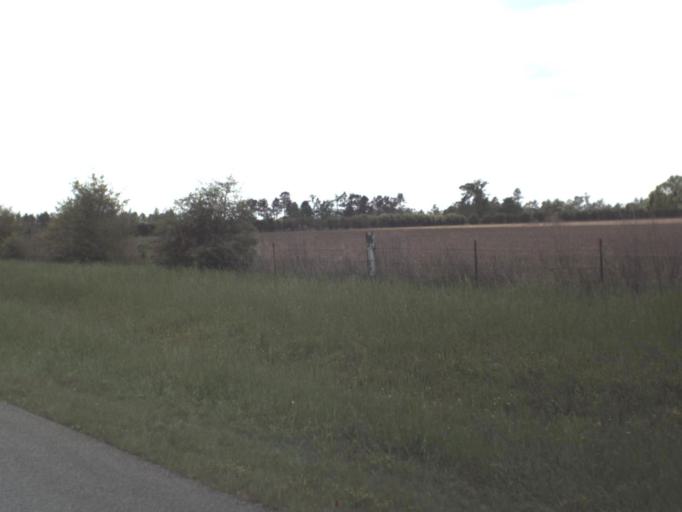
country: US
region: Florida
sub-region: Escambia County
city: Molino
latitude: 30.8059
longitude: -87.4242
